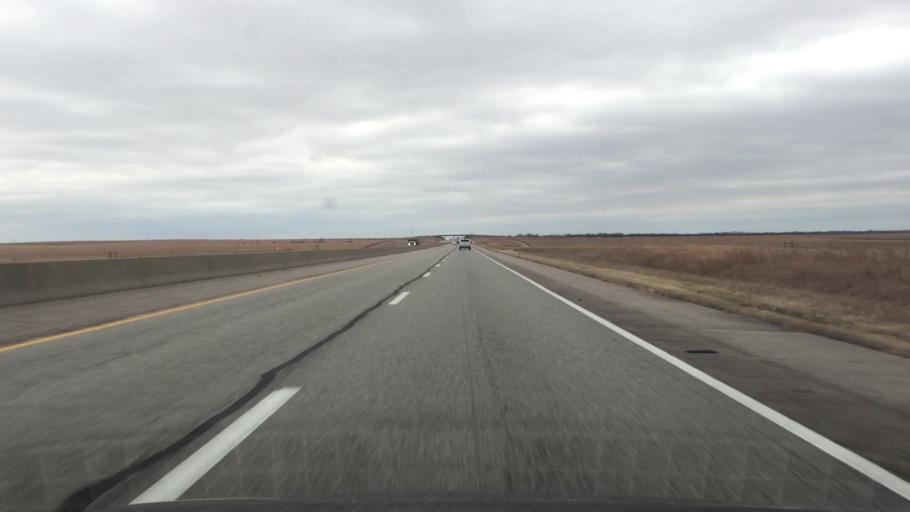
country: US
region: Kansas
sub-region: Butler County
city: El Dorado
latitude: 37.9952
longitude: -96.6961
